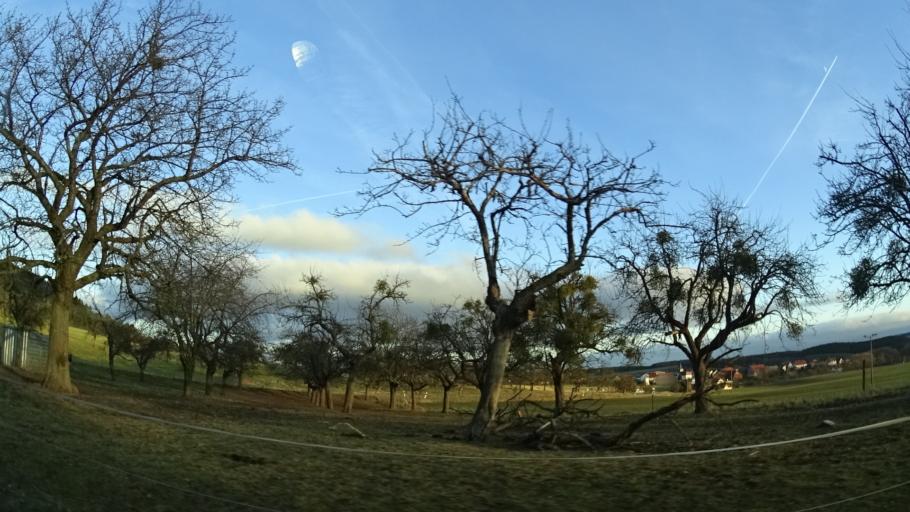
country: DE
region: Thuringia
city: Rudolstadt
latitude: 50.7796
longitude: 11.3735
